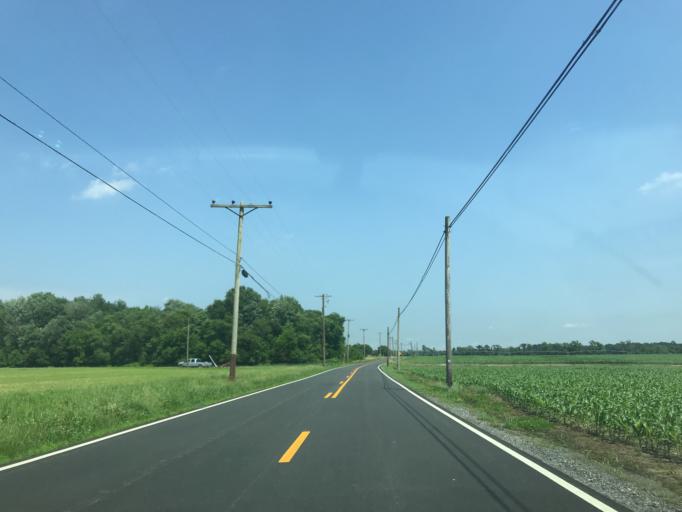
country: US
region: Maryland
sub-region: Dorchester County
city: Hurlock
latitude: 38.5742
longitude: -75.8113
